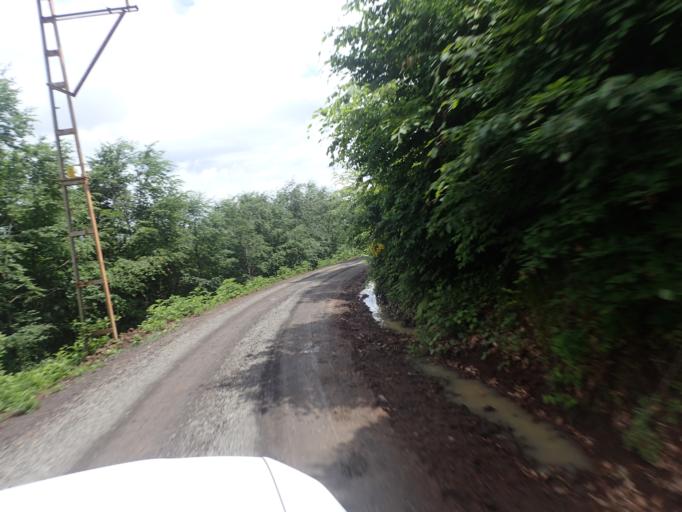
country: TR
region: Ordu
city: Akkus
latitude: 40.9109
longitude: 36.8846
